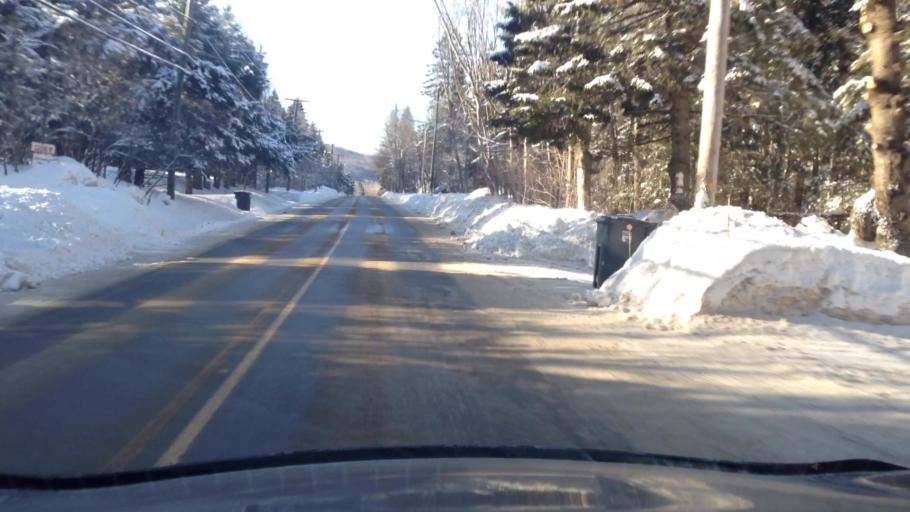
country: CA
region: Quebec
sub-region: Laurentides
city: Sainte-Agathe-des-Monts
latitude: 45.9295
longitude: -74.4094
